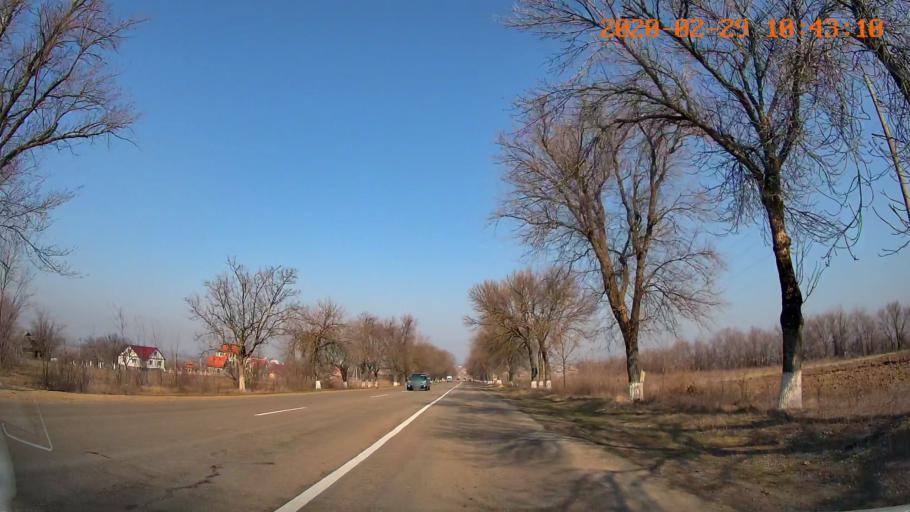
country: MD
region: Telenesti
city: Grigoriopol
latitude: 47.0584
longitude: 29.4047
